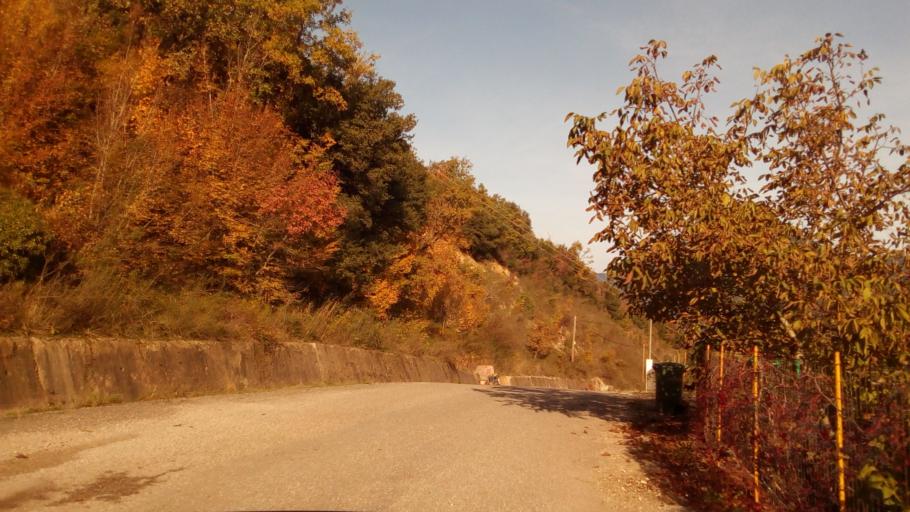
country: GR
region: West Greece
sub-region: Nomos Aitolias kai Akarnanias
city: Thermo
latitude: 38.6544
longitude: 21.8453
